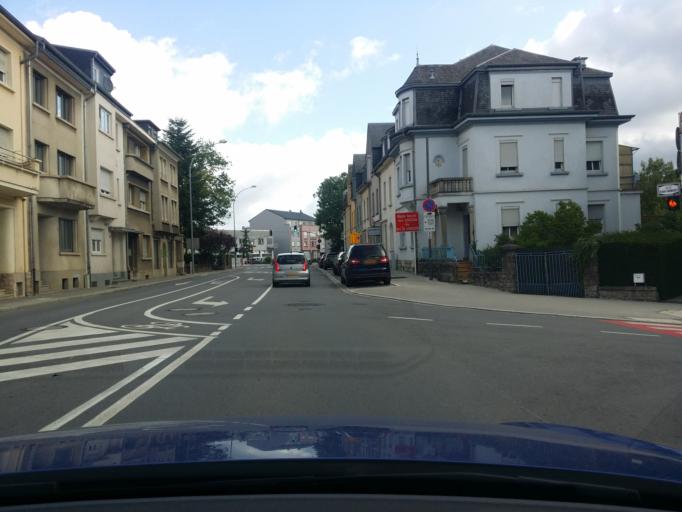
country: LU
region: Luxembourg
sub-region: Canton de Luxembourg
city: Strassen
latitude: 49.6042
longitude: 6.0935
